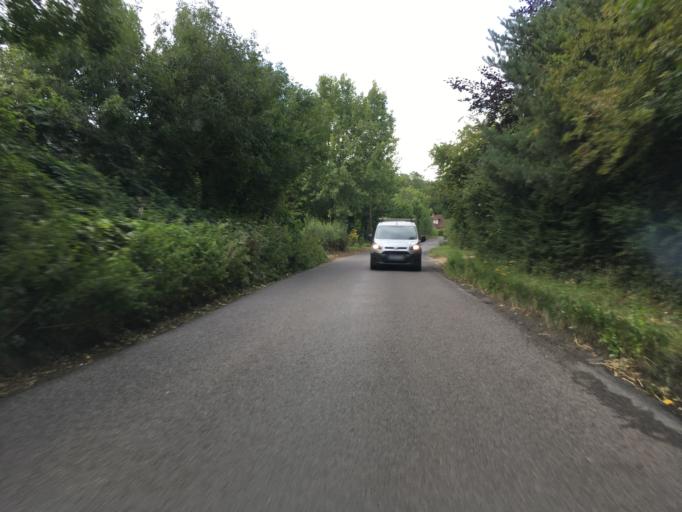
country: GB
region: England
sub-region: Hampshire
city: Colden Common
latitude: 50.9891
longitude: -1.2736
